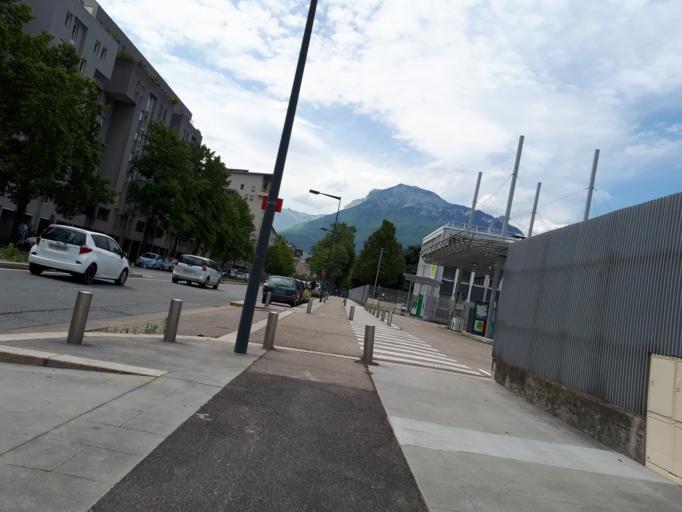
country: FR
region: Rhone-Alpes
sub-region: Departement de l'Isere
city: Saint-Martin-le-Vinoux
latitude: 45.1942
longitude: 5.7100
